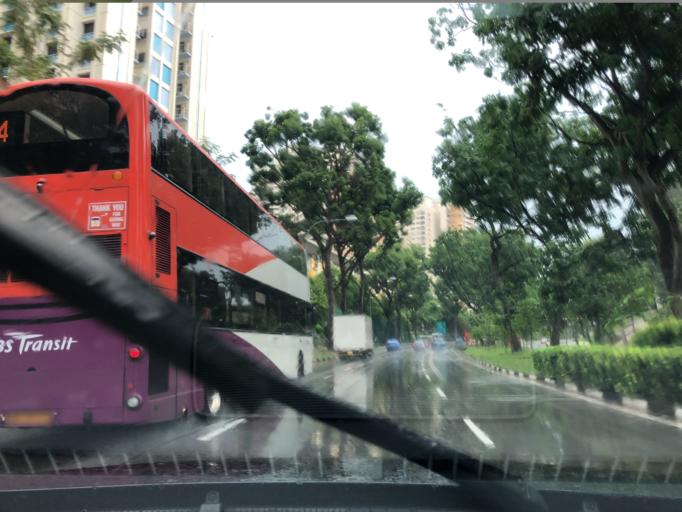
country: SG
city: Singapore
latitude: 1.2860
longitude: 103.8254
